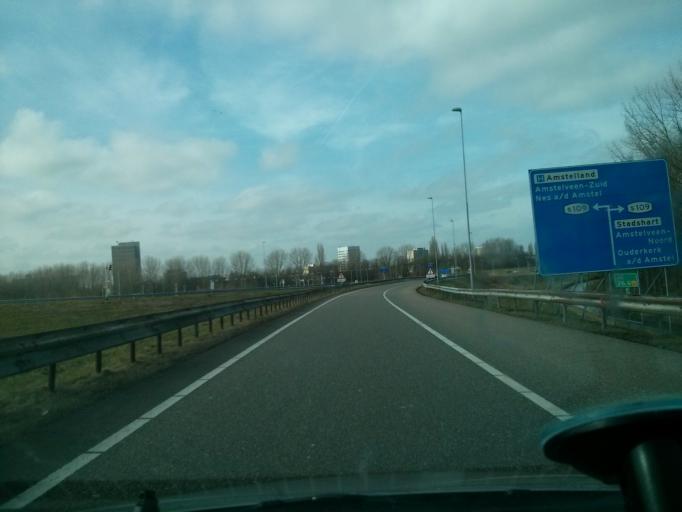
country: NL
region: North Holland
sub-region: Gemeente Amstelveen
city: Amstelveen
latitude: 52.2966
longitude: 4.8851
